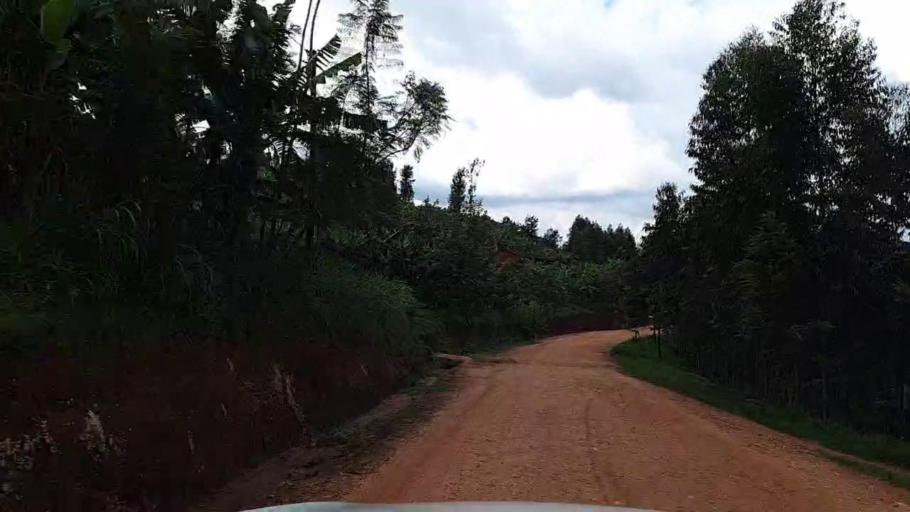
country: RW
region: Southern Province
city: Nyanza
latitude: -2.4118
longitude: 29.6733
